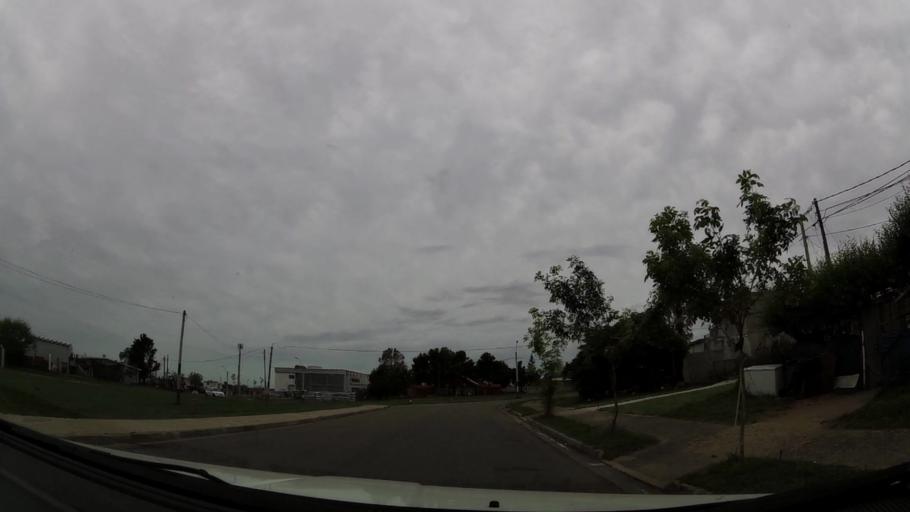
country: UY
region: Maldonado
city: Maldonado
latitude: -34.8935
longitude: -54.9395
